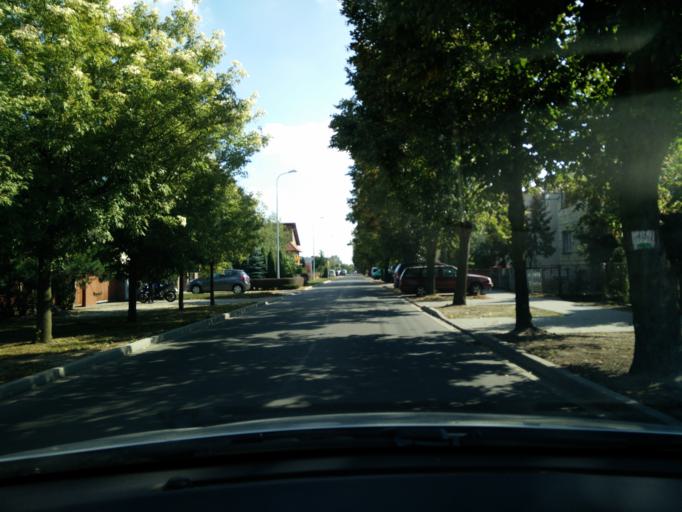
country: PL
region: Greater Poland Voivodeship
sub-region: Powiat sredzki
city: Sroda Wielkopolska
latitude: 52.2365
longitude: 17.2541
